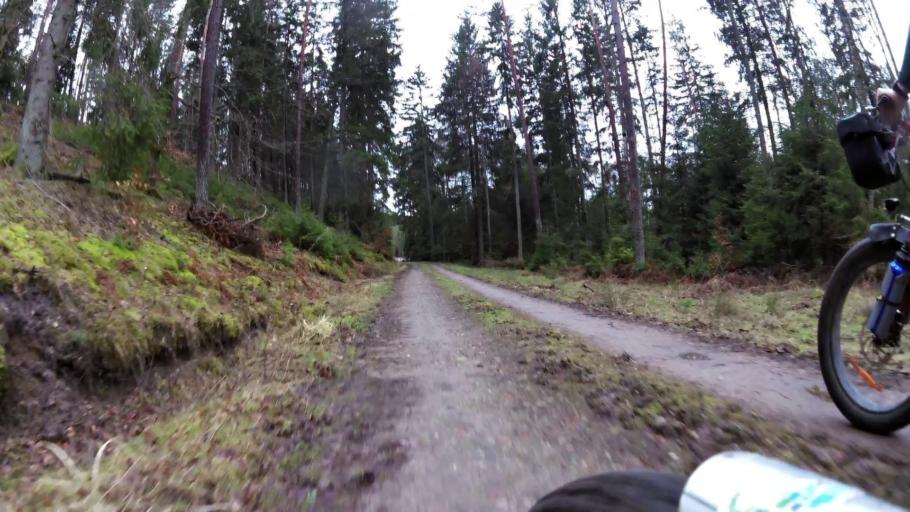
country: PL
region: Pomeranian Voivodeship
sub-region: Powiat bytowski
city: Kolczyglowy
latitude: 54.2521
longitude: 17.3078
